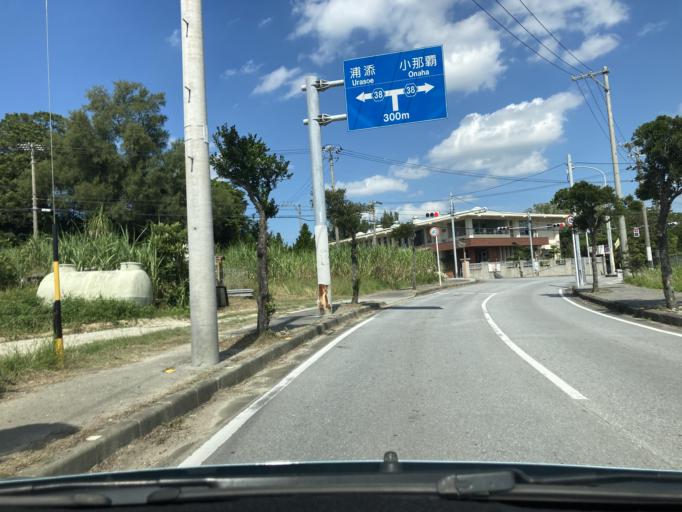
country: JP
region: Okinawa
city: Ginowan
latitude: 26.2287
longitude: 127.7508
